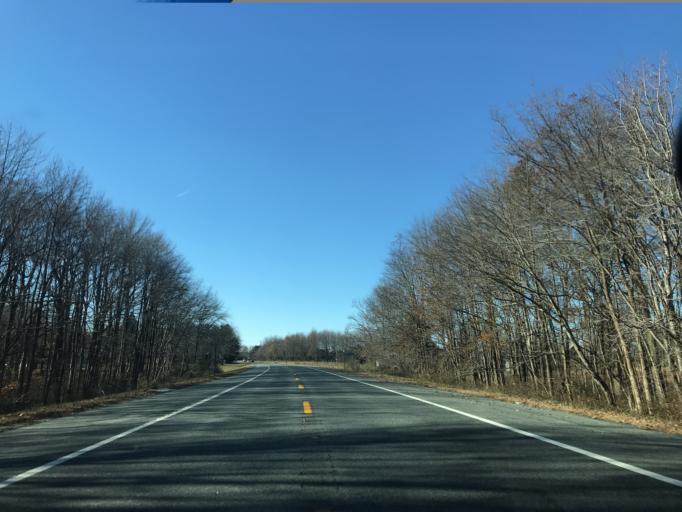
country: US
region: Maryland
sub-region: Harford County
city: Aberdeen
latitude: 39.5784
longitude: -76.1951
